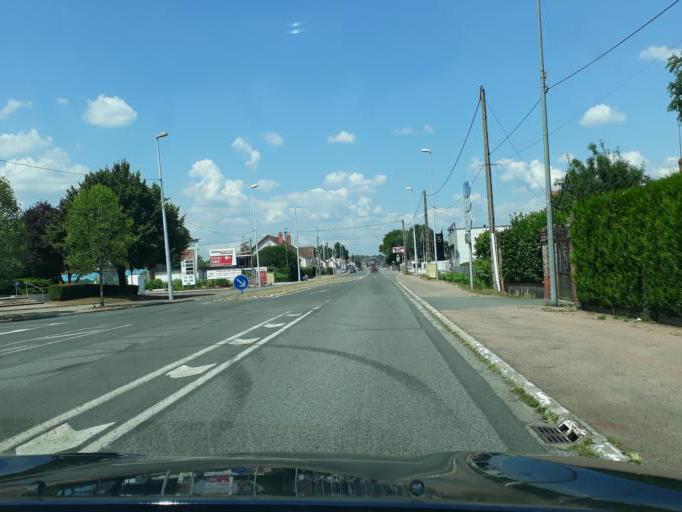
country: FR
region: Bourgogne
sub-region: Departement de la Nievre
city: Challuy
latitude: 46.9607
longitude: 3.1573
